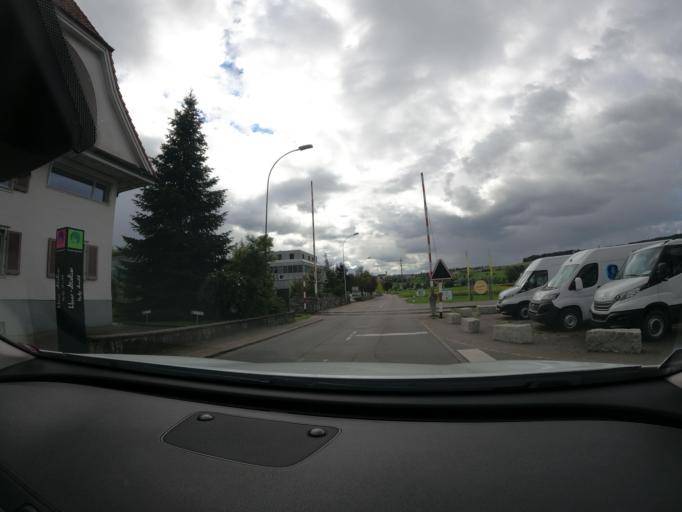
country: CH
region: Lucerne
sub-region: Sursee District
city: Bueron
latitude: 47.2100
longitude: 8.0897
